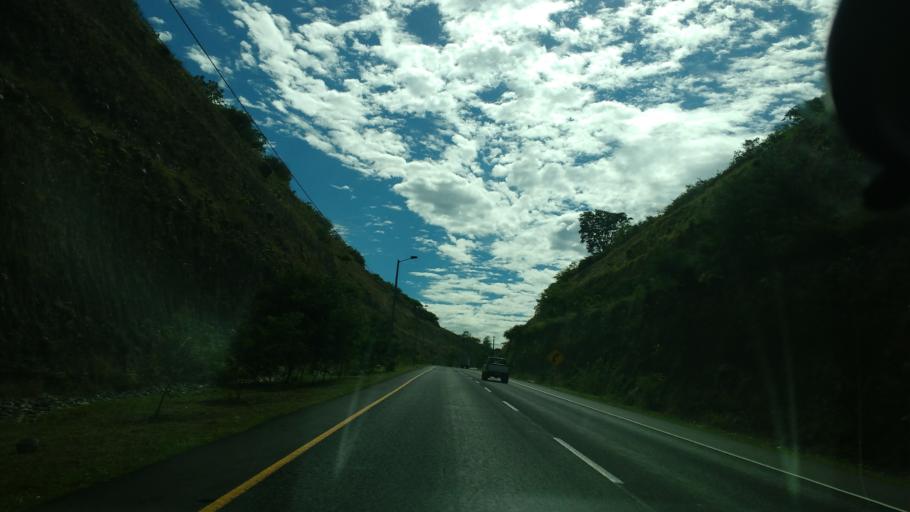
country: CO
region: Tolima
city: Valle de San Juan
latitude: 4.2924
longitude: -75.0381
